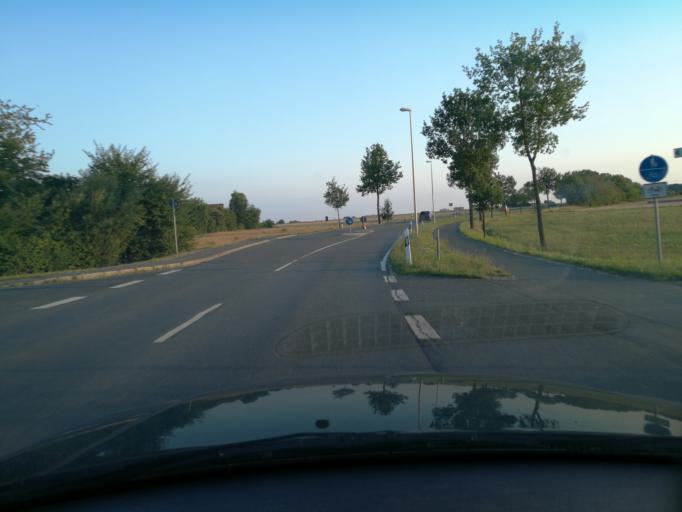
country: DE
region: Bavaria
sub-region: Regierungsbezirk Mittelfranken
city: Herzogenaurach
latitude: 49.5912
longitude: 10.8950
